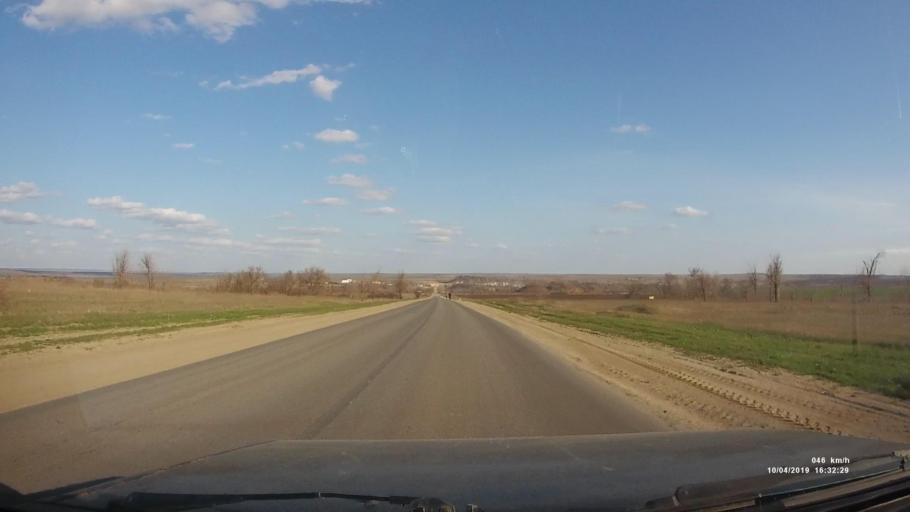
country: RU
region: Rostov
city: Staraya Stanitsa
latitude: 48.2454
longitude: 40.3891
